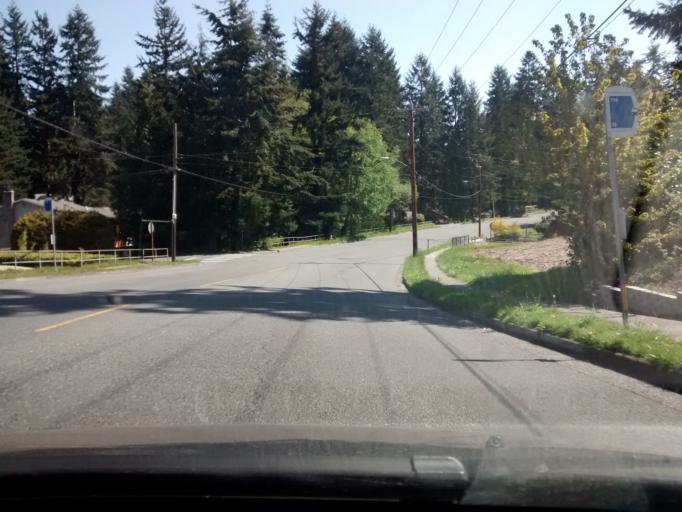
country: US
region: Washington
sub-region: Snohomish County
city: Esperance
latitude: 47.8105
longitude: -122.3510
